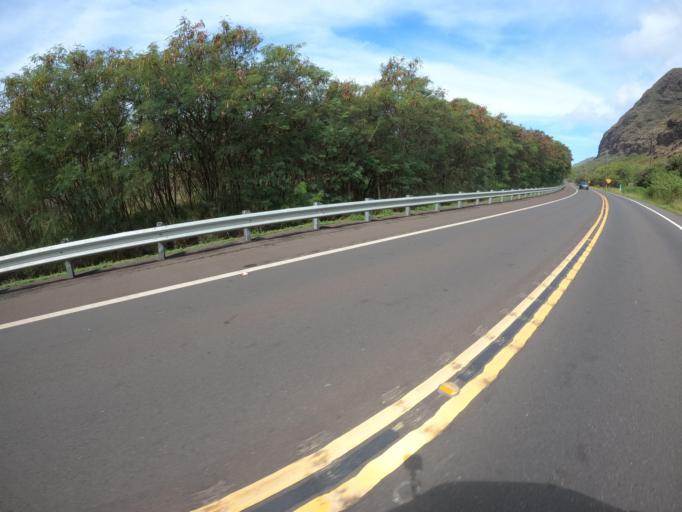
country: US
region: Hawaii
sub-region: Honolulu County
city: Makaha Valley
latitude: 21.5356
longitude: -158.2282
